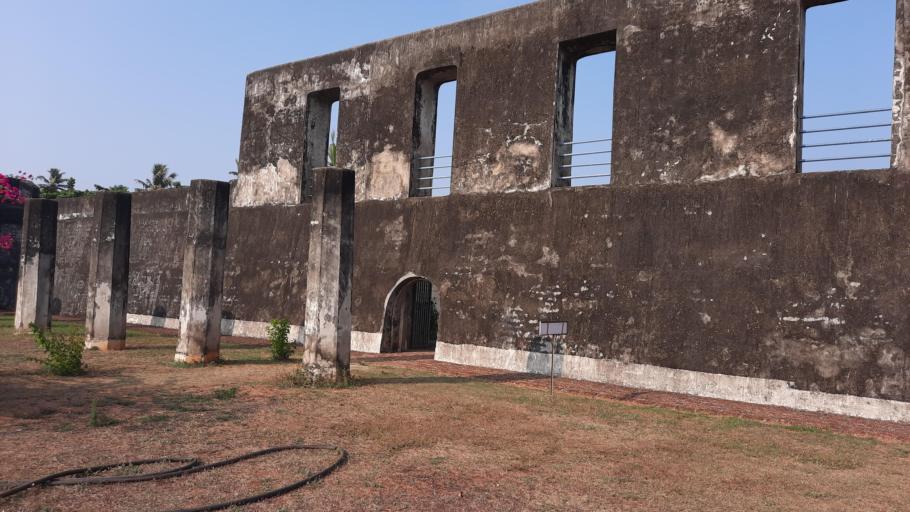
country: IN
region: Kerala
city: Vettur
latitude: 8.6624
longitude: 76.7643
